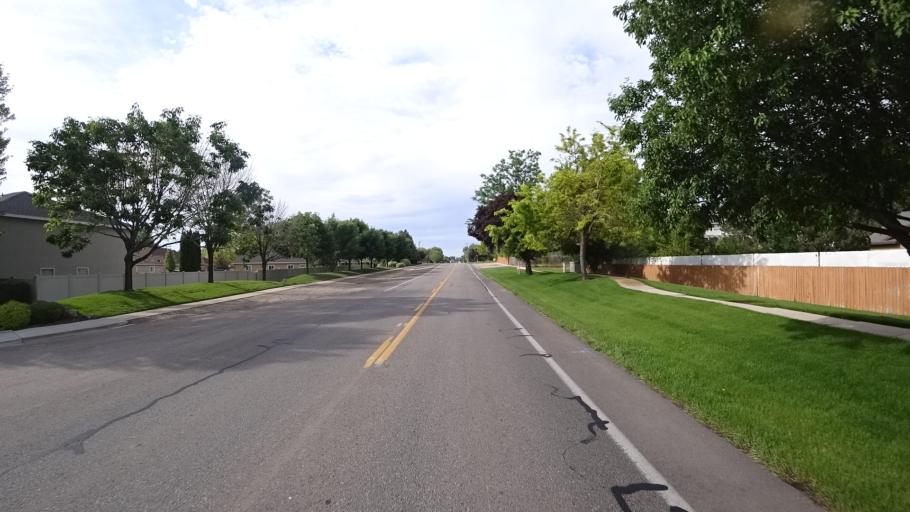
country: US
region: Idaho
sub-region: Ada County
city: Meridian
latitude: 43.5801
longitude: -116.3746
